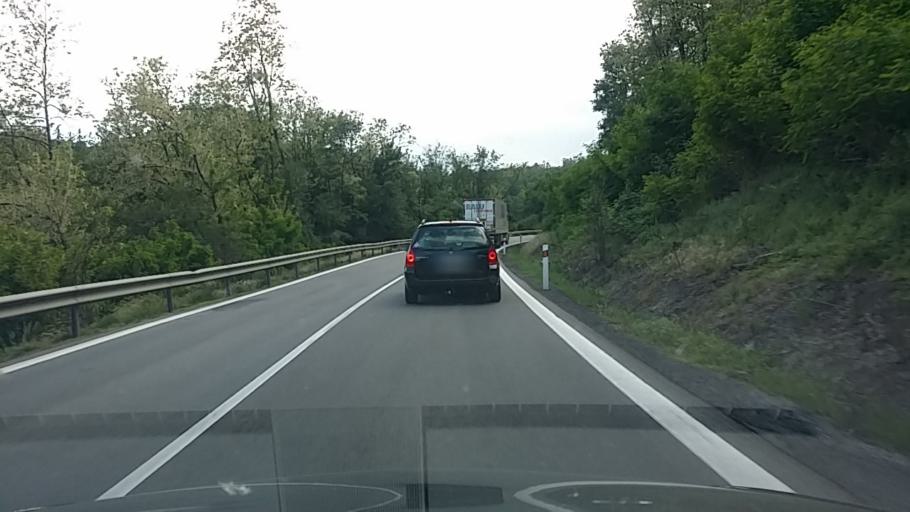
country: SK
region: Banskobystricky
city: Krupina
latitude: 48.3796
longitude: 19.0767
